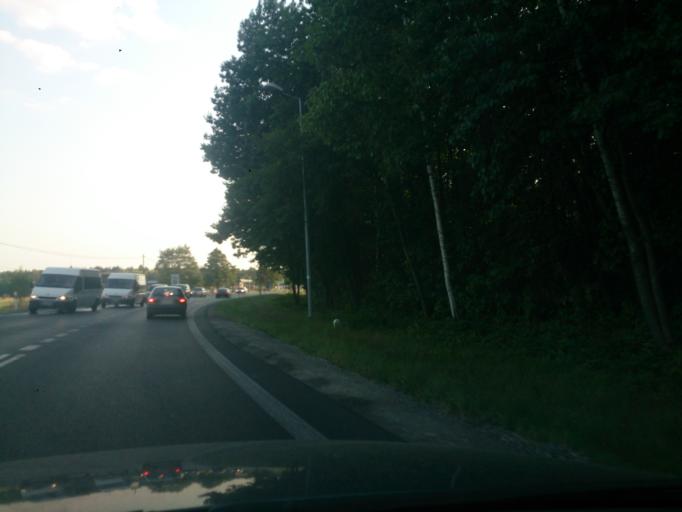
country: PL
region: Subcarpathian Voivodeship
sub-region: Powiat kolbuszowski
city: Majdan Krolewski
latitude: 50.3916
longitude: 21.7619
